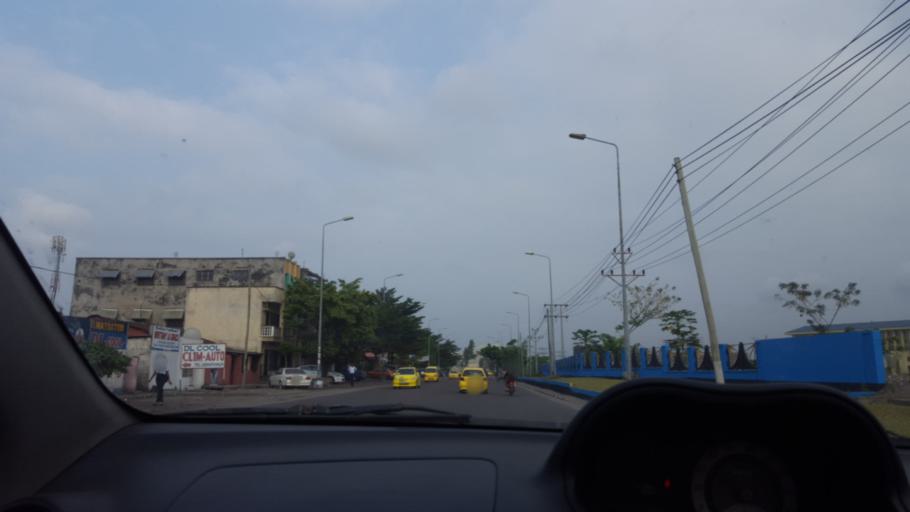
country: CD
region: Kinshasa
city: Kinshasa
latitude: -4.3374
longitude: 15.3029
